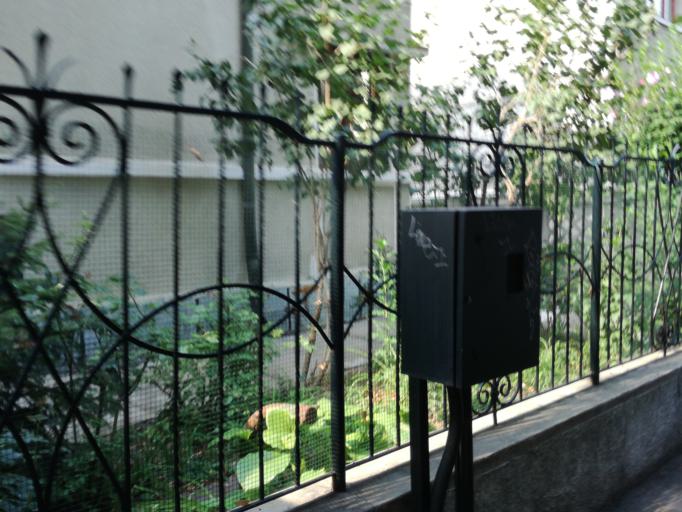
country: RO
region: Bucuresti
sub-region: Municipiul Bucuresti
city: Bucharest
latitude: 44.4588
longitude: 26.1153
